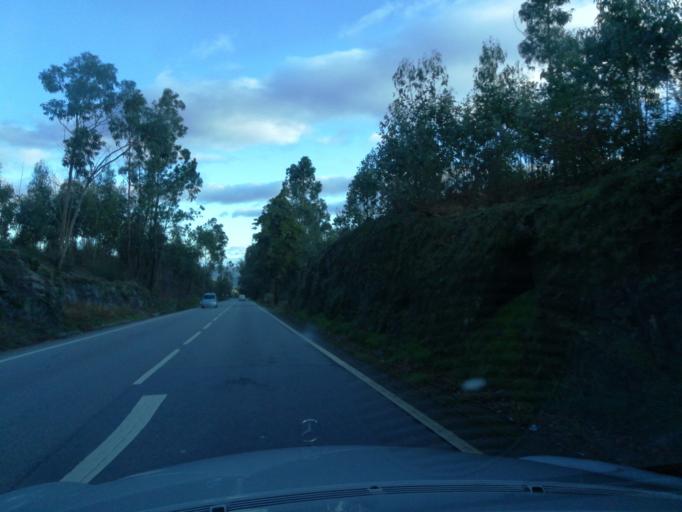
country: PT
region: Braga
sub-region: Barcelos
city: Vila Frescainha
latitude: 41.5677
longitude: -8.6739
